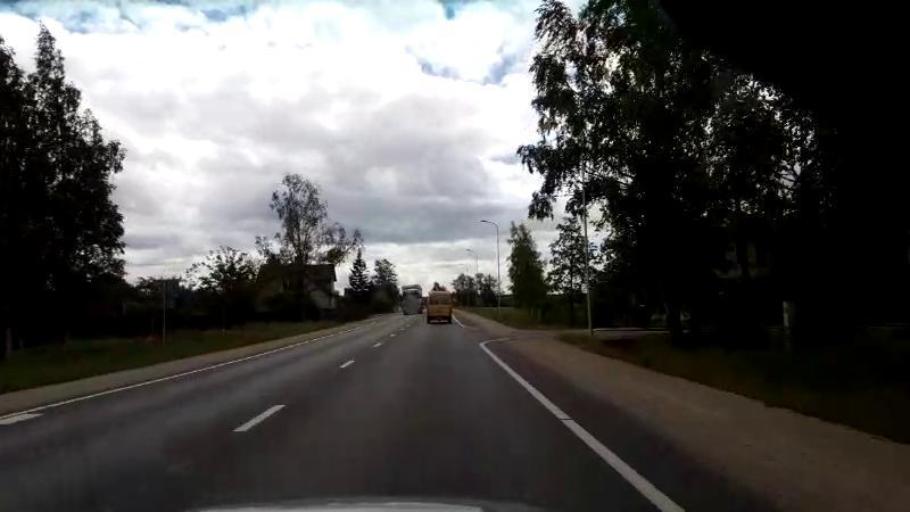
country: LV
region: Salacgrivas
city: Salacgriva
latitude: 57.7454
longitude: 24.3592
